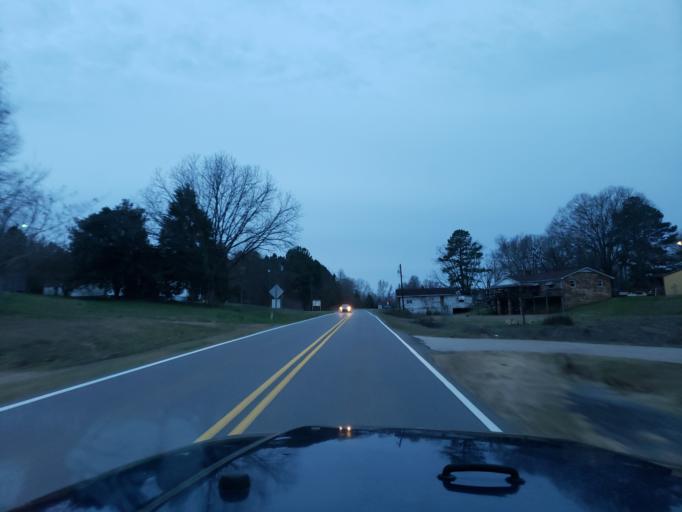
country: US
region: North Carolina
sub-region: Cleveland County
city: White Plains
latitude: 35.2374
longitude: -81.4573
